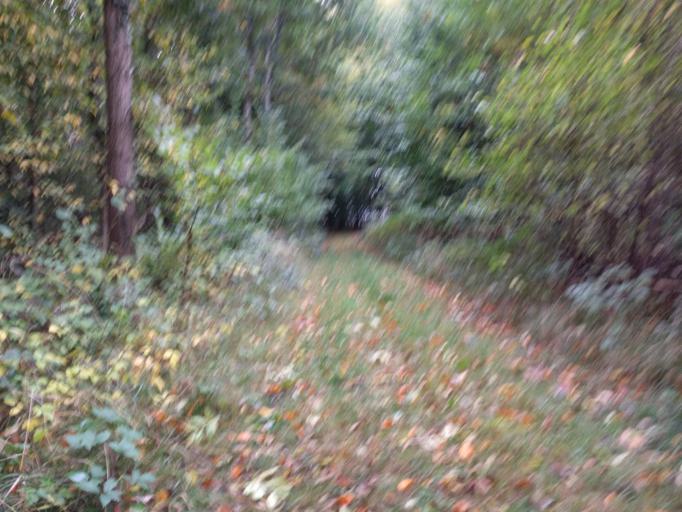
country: DK
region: South Denmark
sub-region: Kerteminde Kommune
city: Langeskov
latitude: 55.4013
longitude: 10.5698
